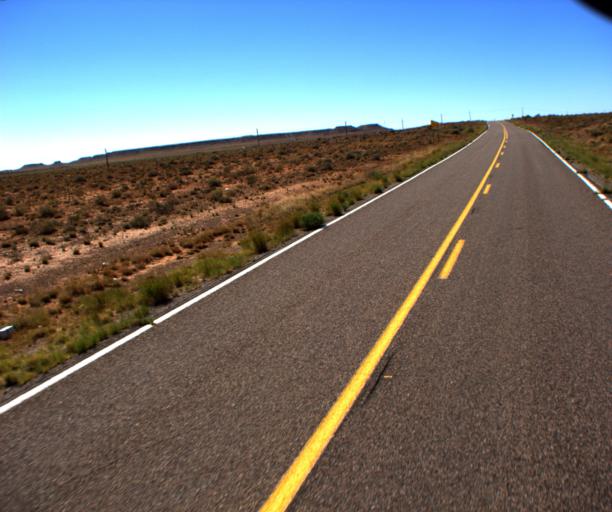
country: US
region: Arizona
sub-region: Coconino County
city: LeChee
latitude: 35.1004
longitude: -110.8631
